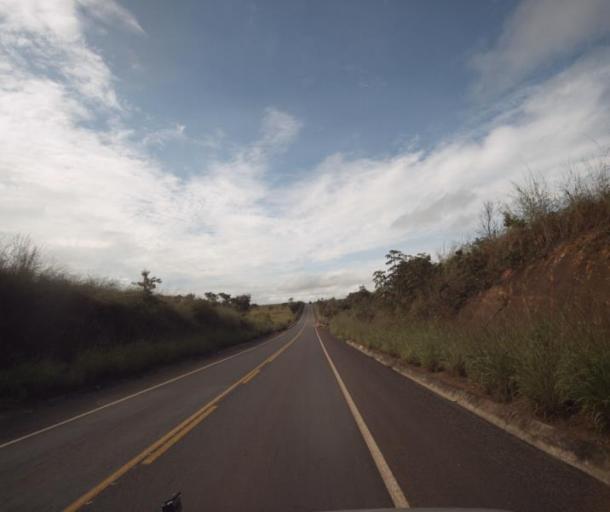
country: BR
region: Goias
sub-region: Padre Bernardo
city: Padre Bernardo
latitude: -15.3943
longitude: -48.6361
